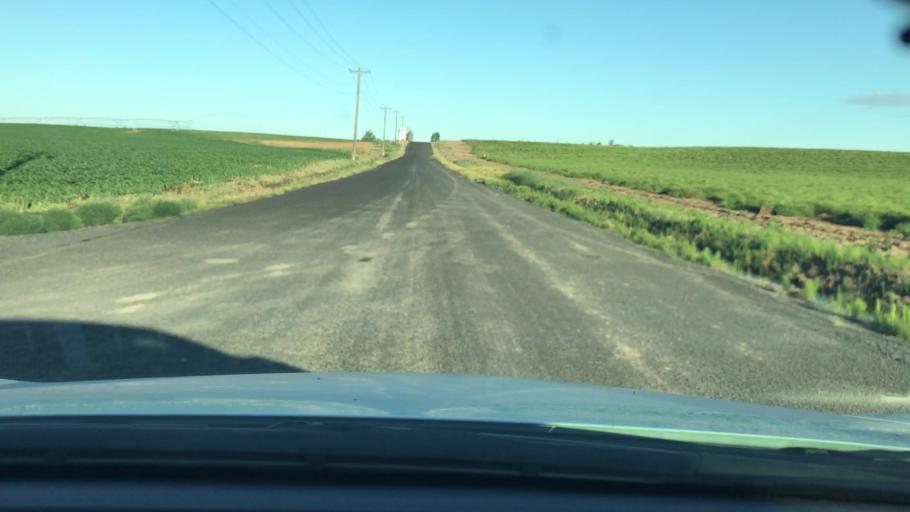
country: US
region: Washington
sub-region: Grant County
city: Moses Lake
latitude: 47.1163
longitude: -119.2254
